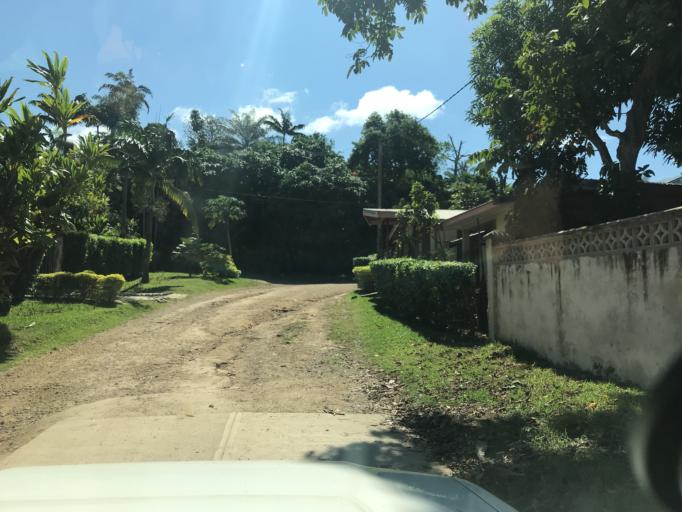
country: VU
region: Sanma
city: Luganville
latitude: -15.5129
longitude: 167.1833
